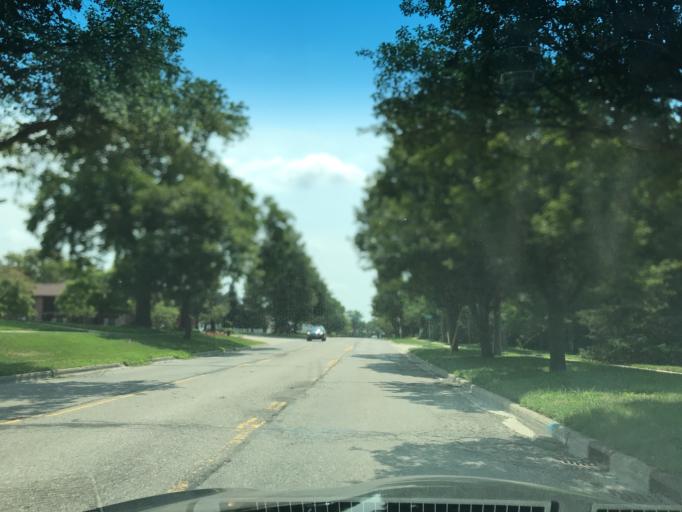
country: US
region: Michigan
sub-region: Oakland County
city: Bingham Farms
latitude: 42.4821
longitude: -83.2795
